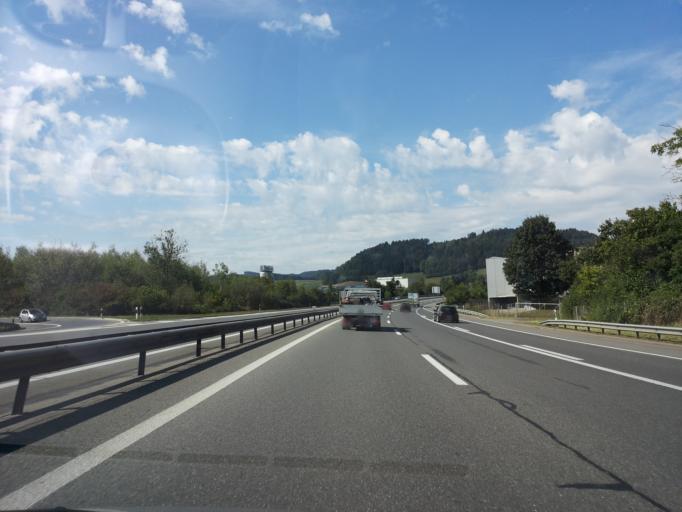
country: CH
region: Lucerne
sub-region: Willisau District
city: Dagmersellen
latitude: 47.2088
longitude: 7.9824
